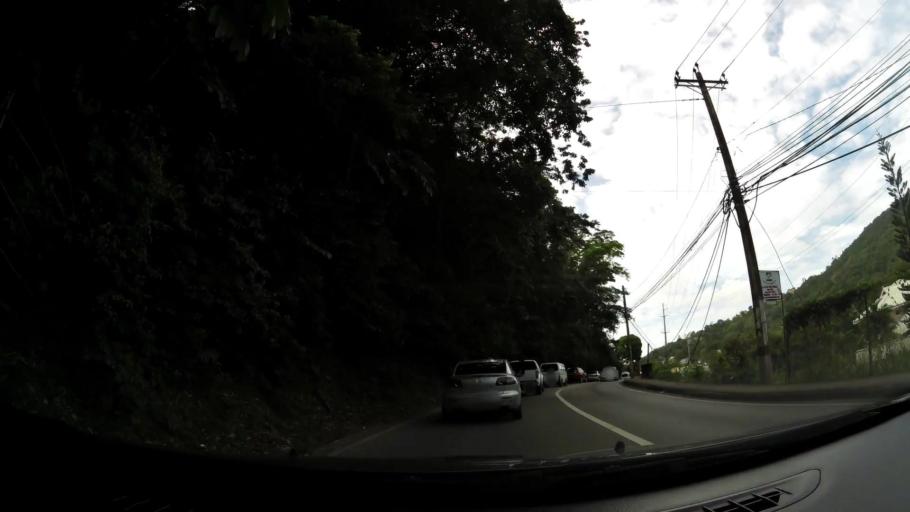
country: TT
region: Diego Martin
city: Petit Valley
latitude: 10.6906
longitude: -61.5187
